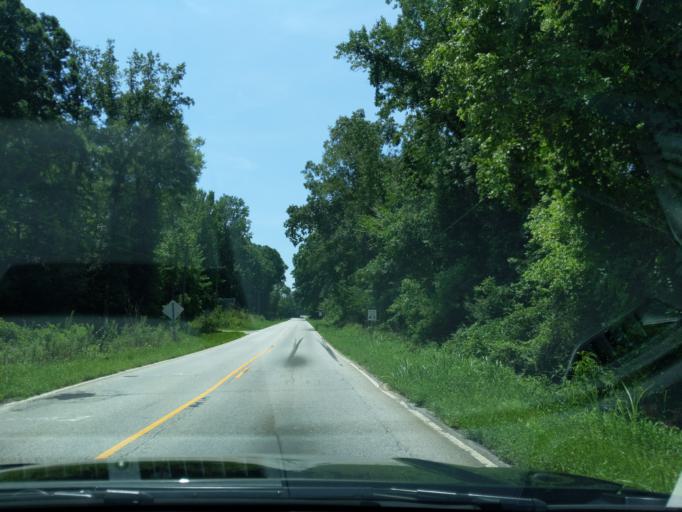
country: US
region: South Carolina
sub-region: Laurens County
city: Laurens
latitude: 34.4753
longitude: -82.0282
